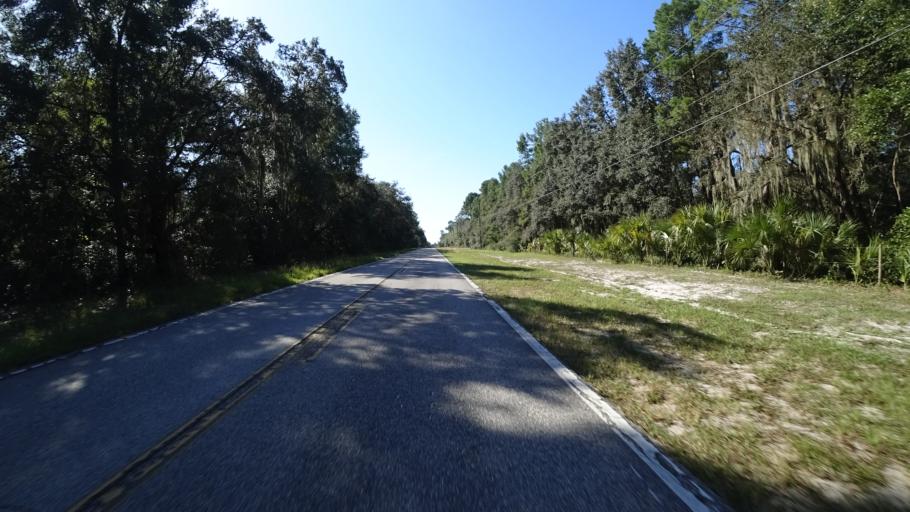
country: US
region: Florida
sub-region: Hillsborough County
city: Wimauma
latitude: 27.6589
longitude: -82.2942
